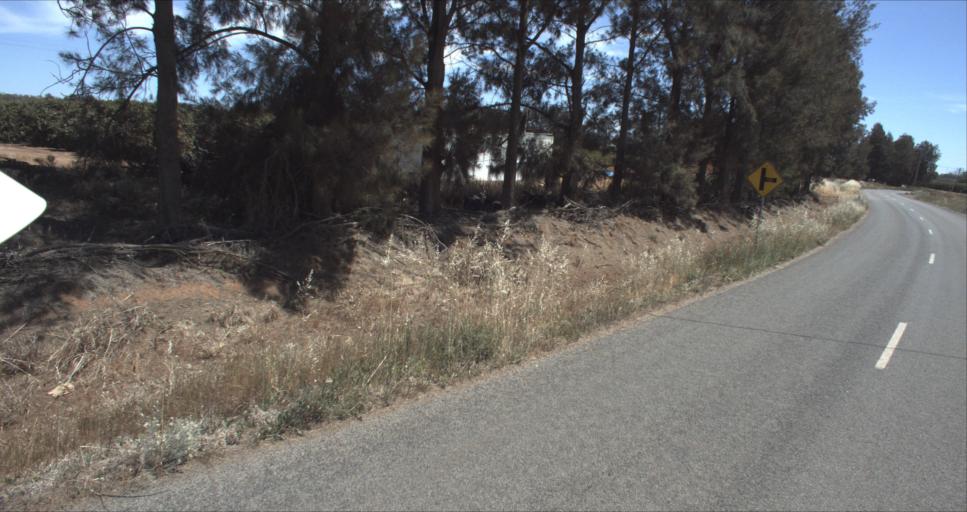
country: AU
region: New South Wales
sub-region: Leeton
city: Leeton
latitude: -34.5918
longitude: 146.4654
